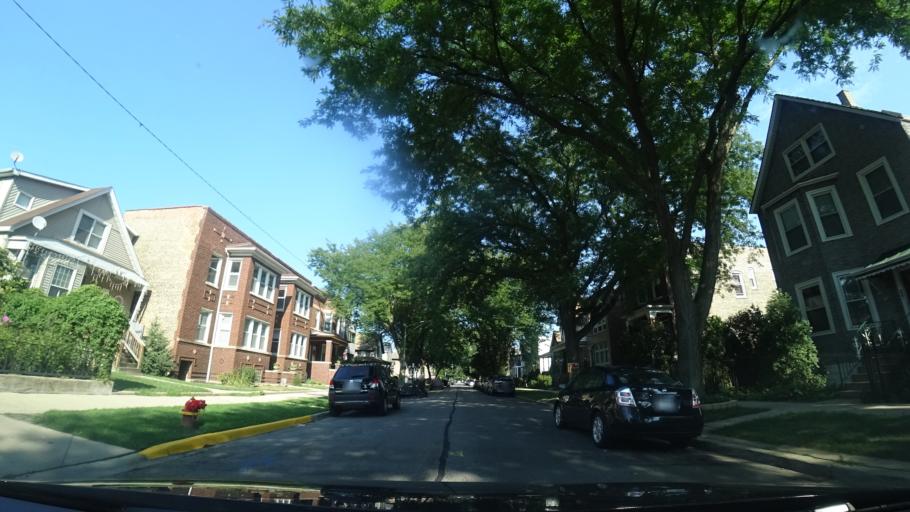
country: US
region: Illinois
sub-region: Cook County
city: Lincolnwood
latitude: 41.9748
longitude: -87.6947
